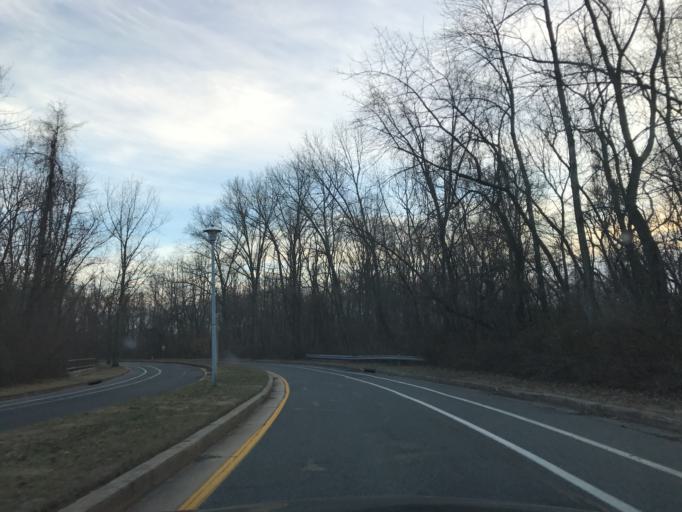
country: US
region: Maryland
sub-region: Harford County
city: Joppatowne
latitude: 39.4182
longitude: -76.3688
